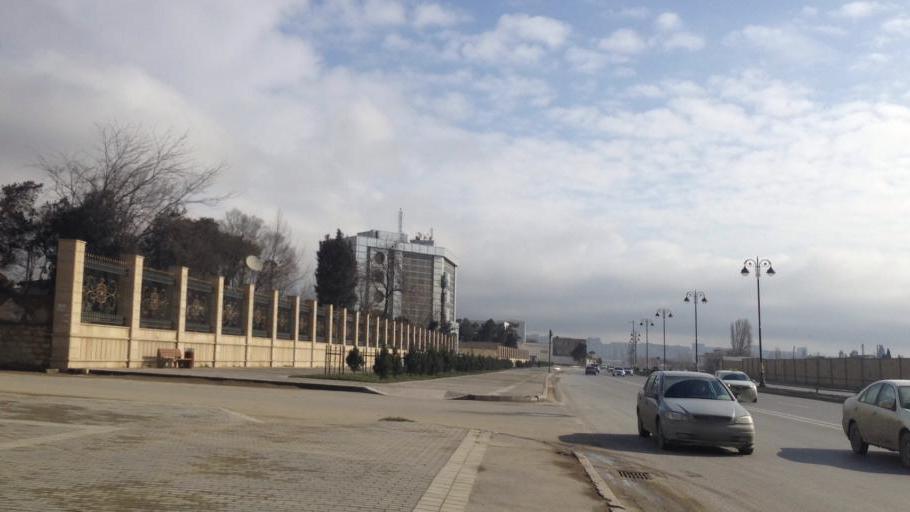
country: AZ
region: Baki
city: Baku
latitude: 40.3781
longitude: 49.8933
